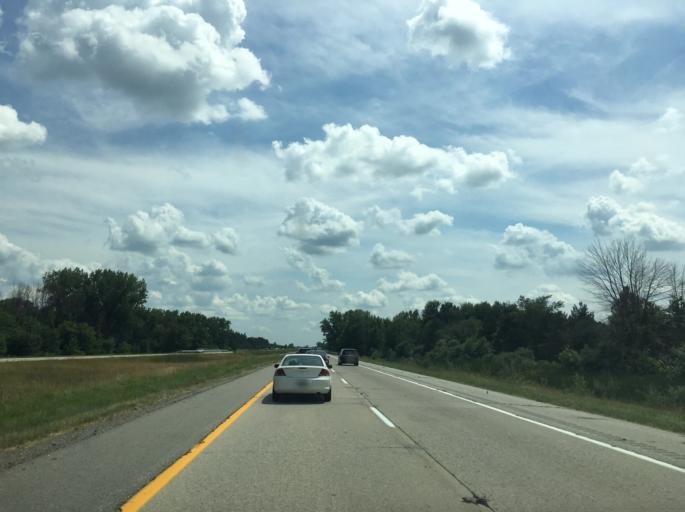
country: US
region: Michigan
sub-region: Bay County
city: Auburn
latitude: 43.7004
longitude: -84.0128
